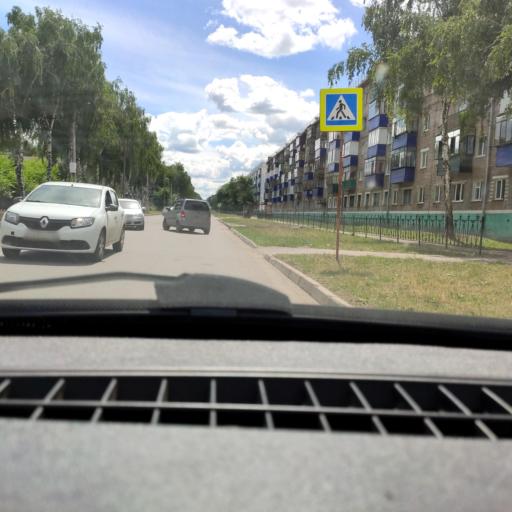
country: RU
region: Bashkortostan
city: Sterlitamak
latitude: 53.6399
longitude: 55.9314
